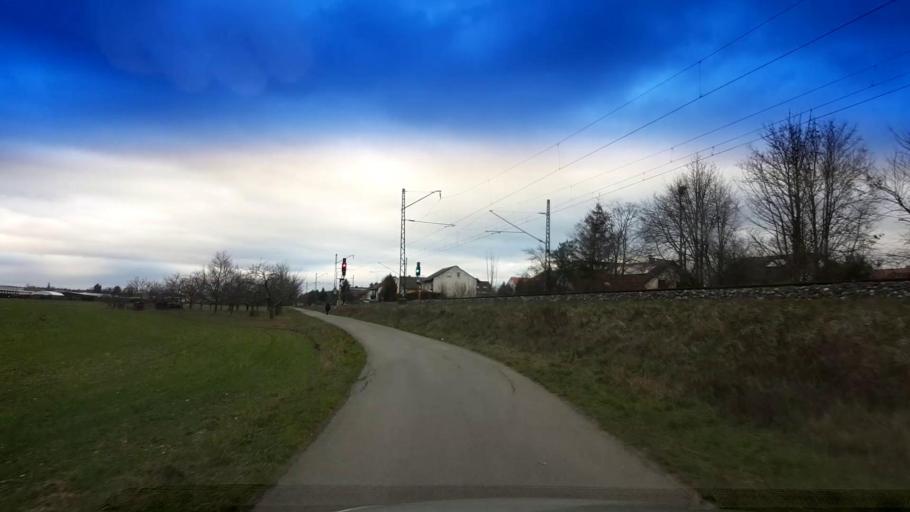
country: DE
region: Bavaria
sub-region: Upper Franconia
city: Strullendorf
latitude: 49.8391
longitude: 10.9688
